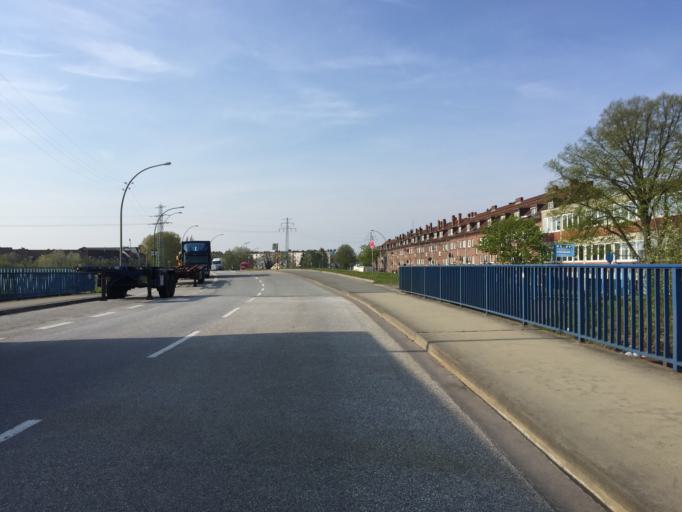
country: DE
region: Hamburg
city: Kleiner Grasbrook
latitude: 53.5224
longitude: 9.9823
